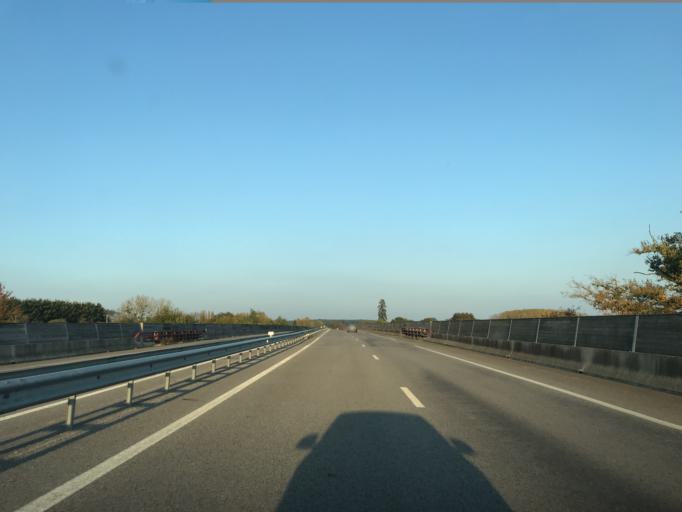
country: FR
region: Lower Normandy
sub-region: Departement de l'Orne
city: Valframbert
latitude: 48.4762
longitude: 0.2076
